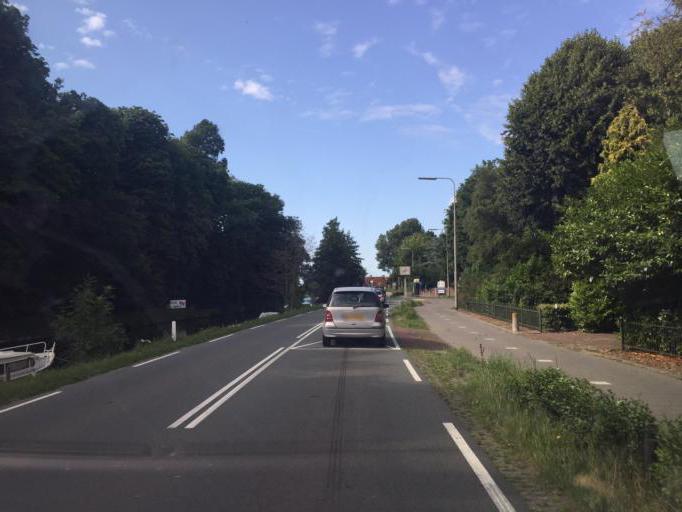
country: NL
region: South Holland
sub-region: Gemeente Teylingen
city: Voorhout
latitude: 52.2160
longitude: 4.4784
